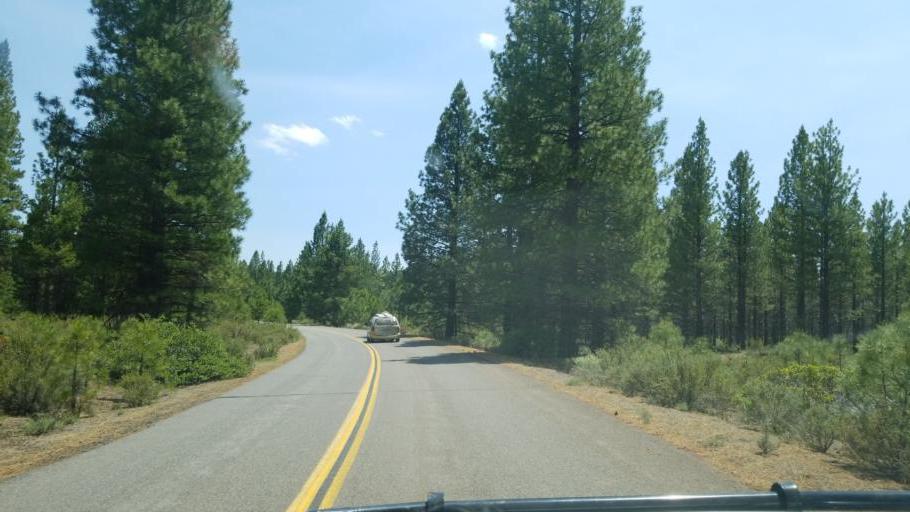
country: US
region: California
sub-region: Lassen County
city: Susanville
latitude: 40.5700
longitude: -120.8429
